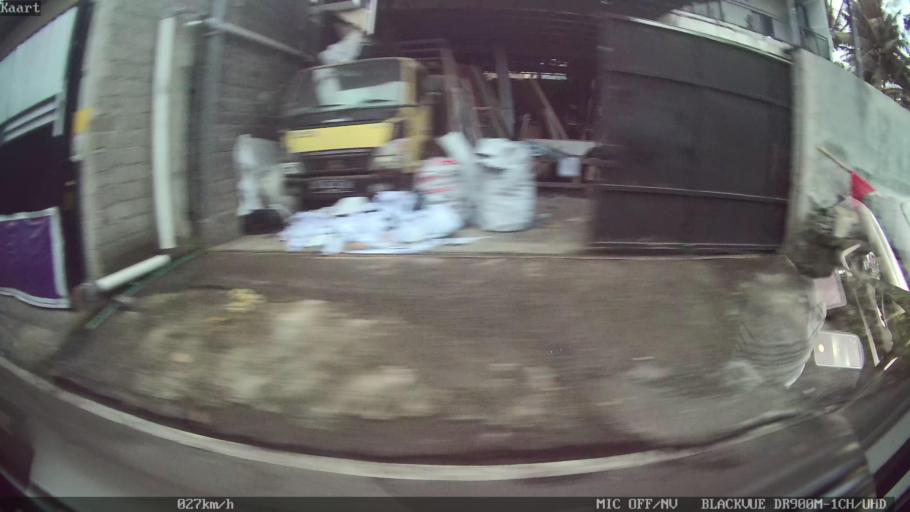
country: ID
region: Bali
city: Banjar Parekan
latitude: -8.5641
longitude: 115.2135
